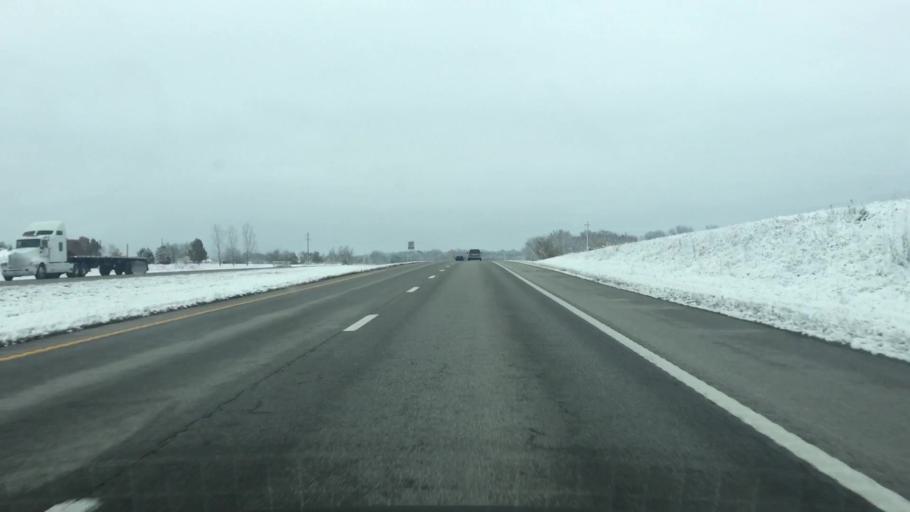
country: US
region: Missouri
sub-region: Cass County
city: Garden City
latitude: 38.5325
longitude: -94.1529
